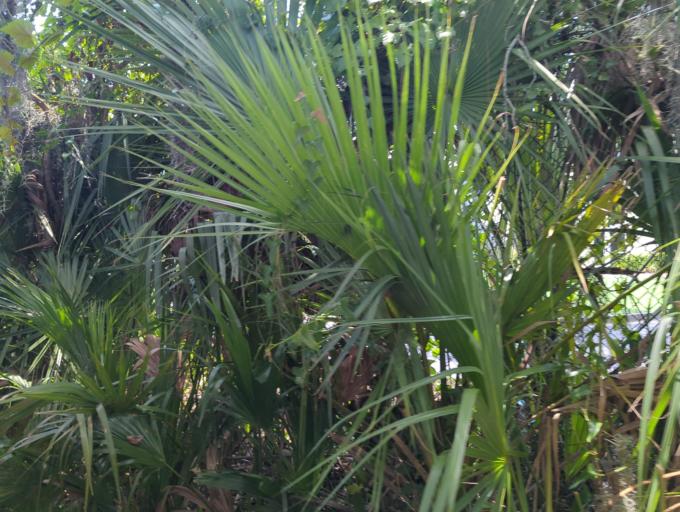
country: US
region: Florida
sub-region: Duval County
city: Jacksonville
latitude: 30.4012
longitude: -81.6461
